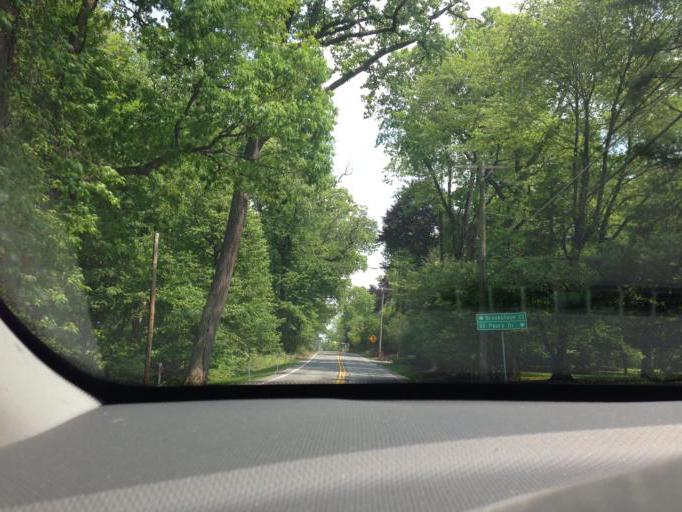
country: US
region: Maryland
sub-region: Baltimore County
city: Mays Chapel
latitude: 39.4339
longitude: -76.6793
